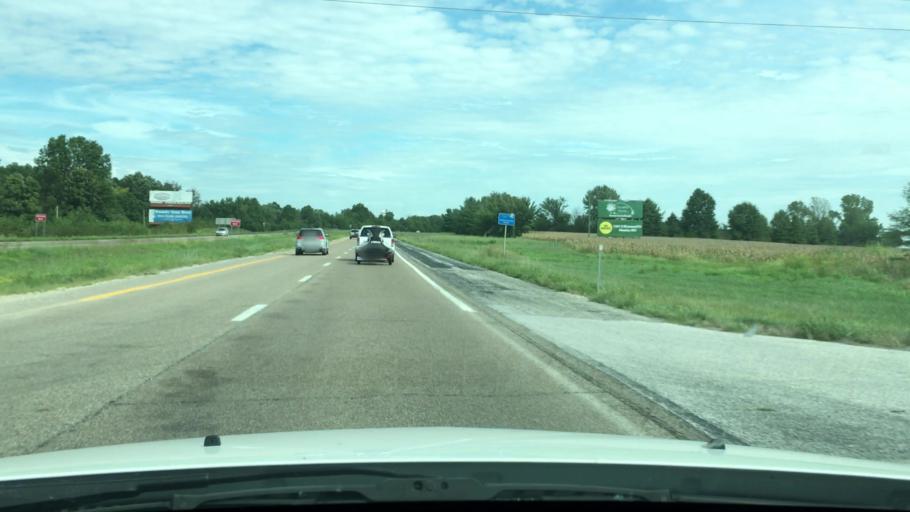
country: US
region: Missouri
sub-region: Callaway County
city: Fulton
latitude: 39.0034
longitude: -91.8930
